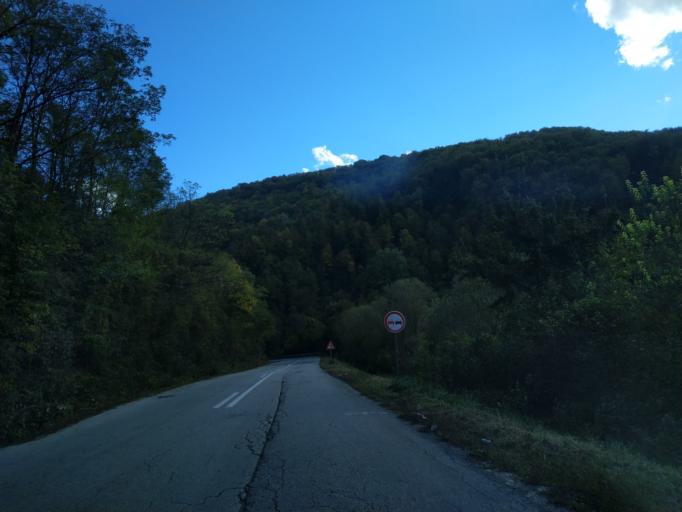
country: RS
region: Central Serbia
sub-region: Zlatiborski Okrug
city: Uzice
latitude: 43.8805
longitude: 19.7791
